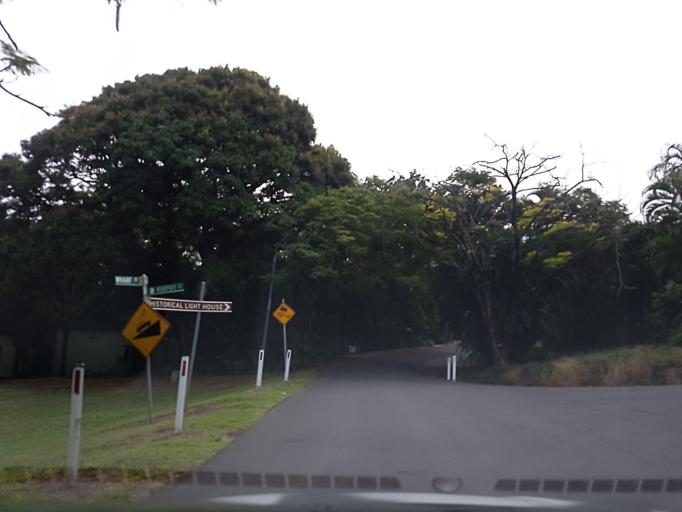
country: AU
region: Queensland
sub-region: Cairns
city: Port Douglas
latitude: -16.4796
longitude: 145.4630
